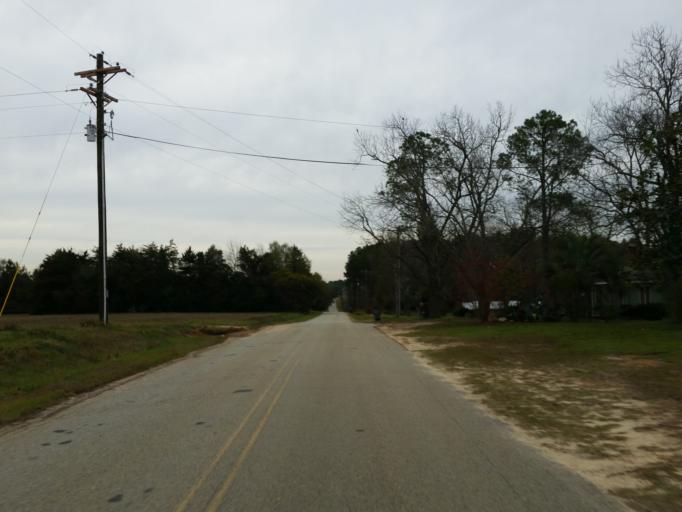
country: US
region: Georgia
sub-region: Crisp County
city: Cordele
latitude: 31.9189
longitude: -83.7283
